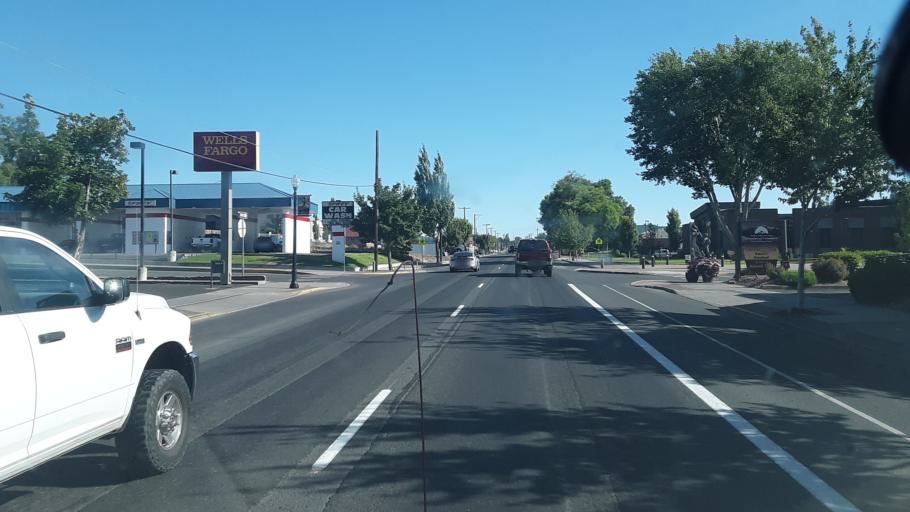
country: US
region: Oregon
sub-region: Jefferson County
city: Madras
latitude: 44.6324
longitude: -121.1306
